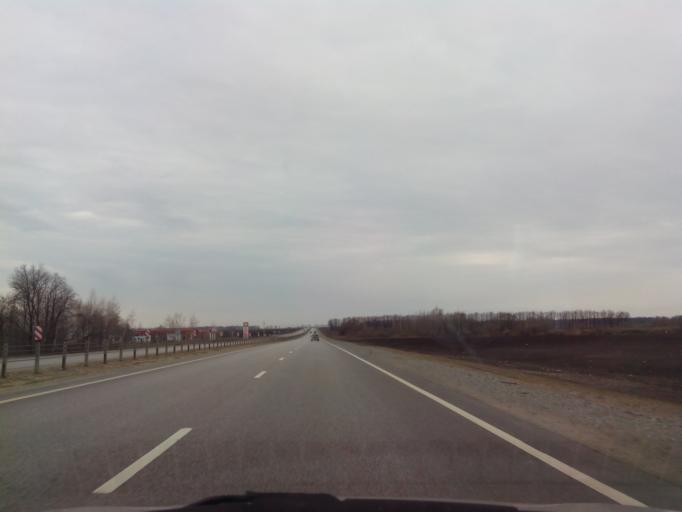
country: RU
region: Tambov
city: Zavoronezhskoye
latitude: 52.8997
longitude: 40.6655
